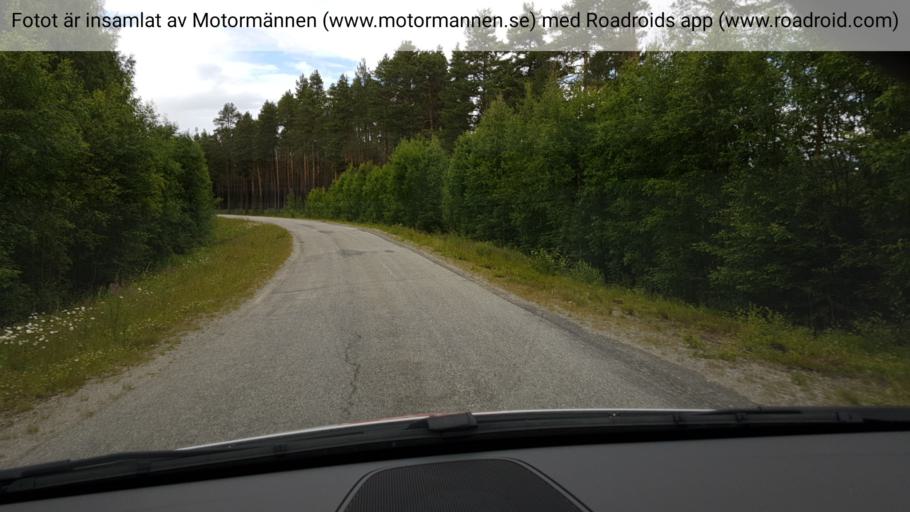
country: SE
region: Vaesterbotten
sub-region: Dorotea Kommun
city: Dorotea
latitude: 63.9181
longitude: 16.2644
